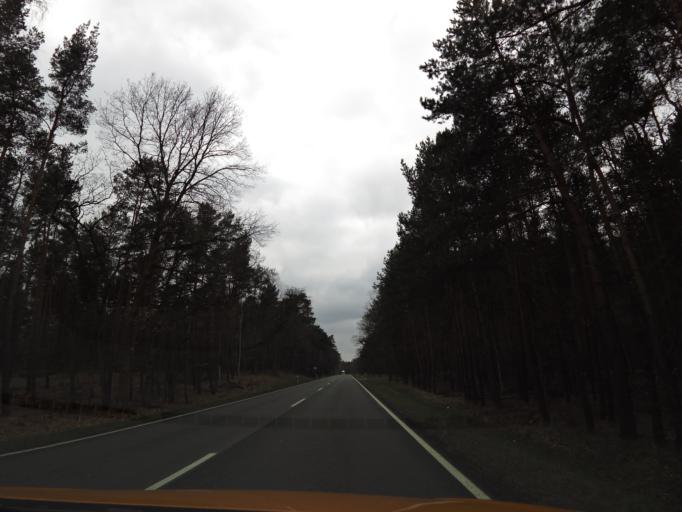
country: DE
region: Brandenburg
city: Nennhausen
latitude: 52.6115
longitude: 12.4244
